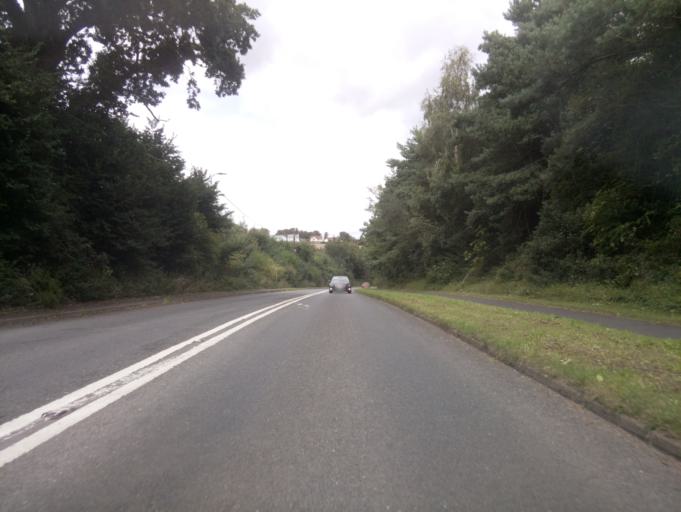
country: GB
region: England
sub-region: Devon
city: Dawlish
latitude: 50.5663
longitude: -3.4762
